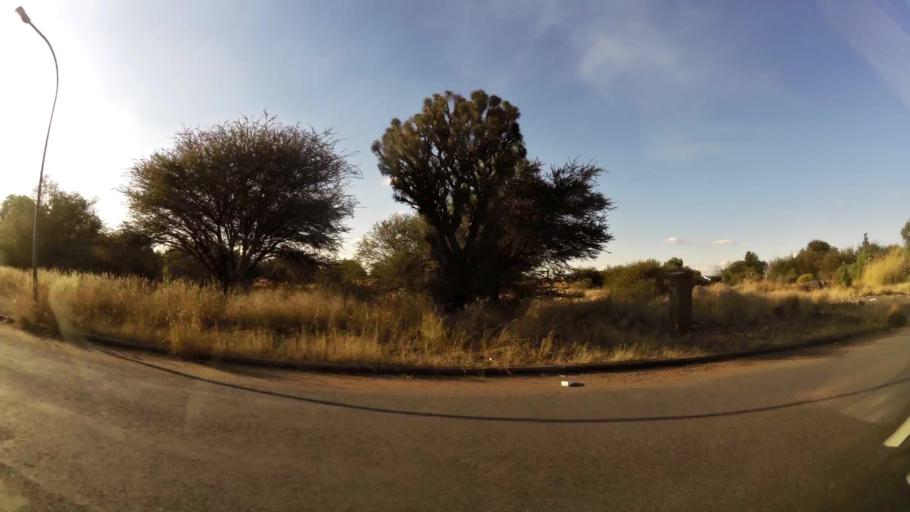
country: ZA
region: Northern Cape
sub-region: Frances Baard District Municipality
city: Kimberley
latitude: -28.7373
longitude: 24.7515
